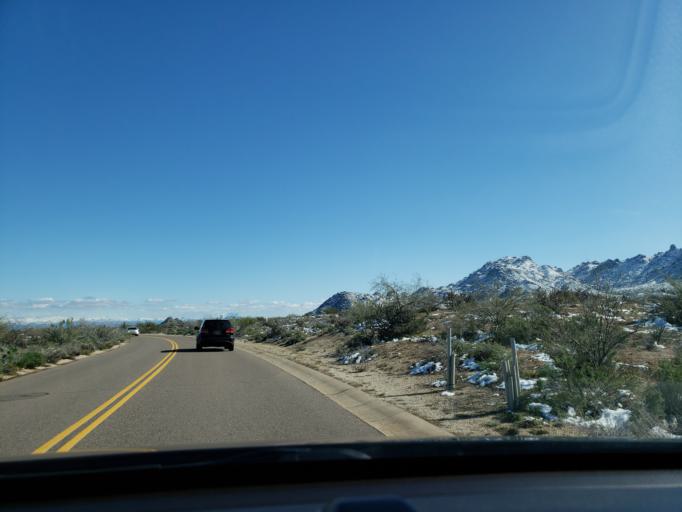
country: US
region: Arizona
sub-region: Maricopa County
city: Rio Verde
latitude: 33.7135
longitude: -111.8144
